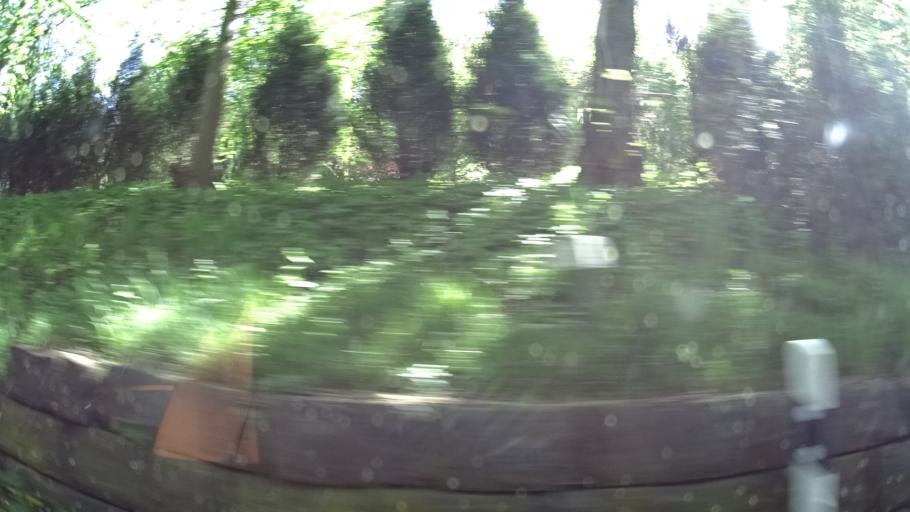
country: DE
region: Baden-Wuerttemberg
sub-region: Karlsruhe Region
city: Hofen an der Enz
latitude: 48.8152
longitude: 8.5794
